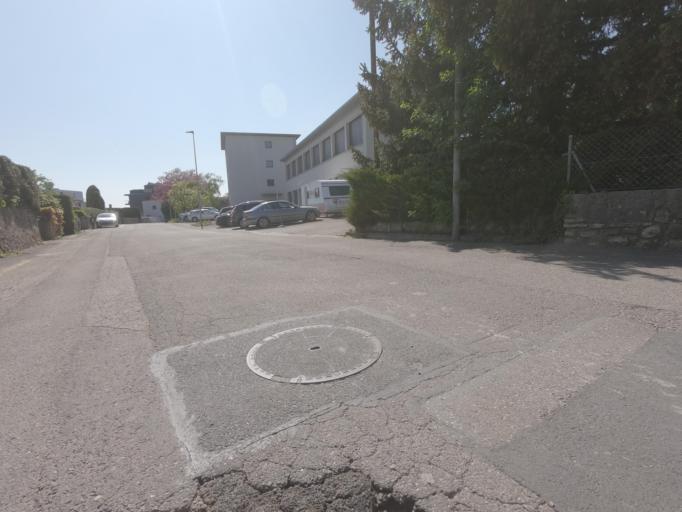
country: CH
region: Bern
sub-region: Jura bernois
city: La Neuveville
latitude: 47.0662
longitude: 7.1068
